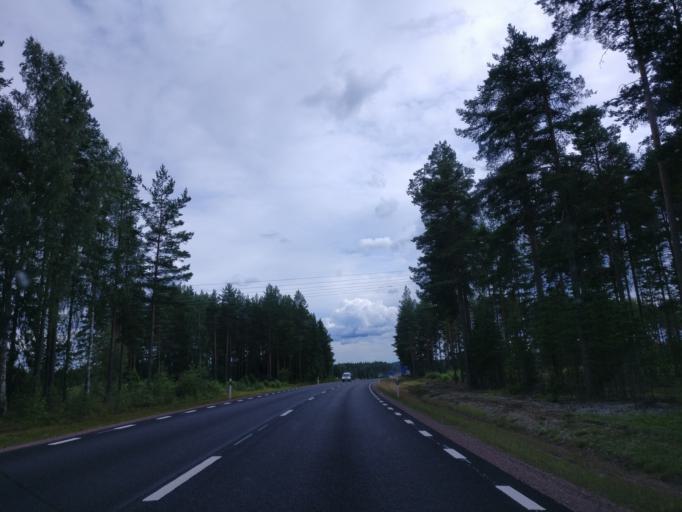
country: SE
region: Vaermland
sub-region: Hagfors Kommun
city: Hagfors
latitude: 60.0397
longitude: 13.5858
